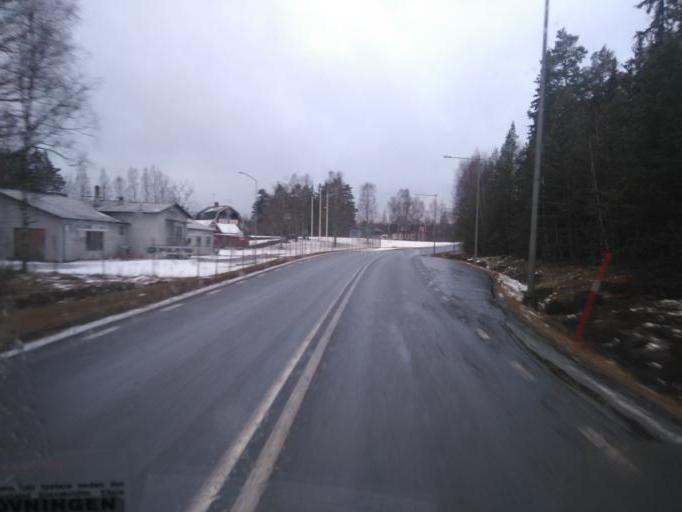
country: SE
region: Joenkoeping
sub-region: Eksjo Kommun
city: Mariannelund
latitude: 57.6197
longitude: 15.5891
